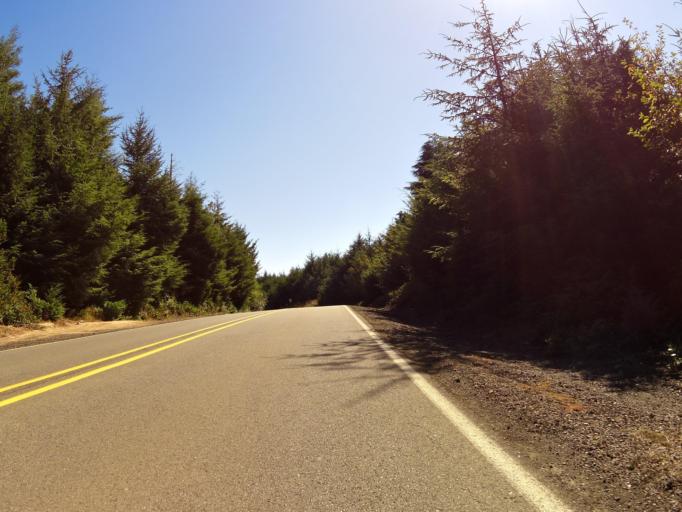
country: US
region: Oregon
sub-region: Coos County
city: Barview
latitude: 43.2715
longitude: -124.3542
